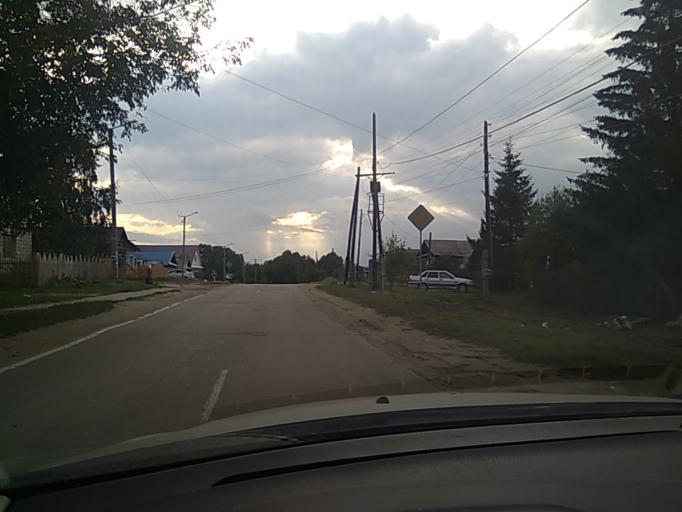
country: RU
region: Chelyabinsk
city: Kyshtym
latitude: 55.6969
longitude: 60.5471
